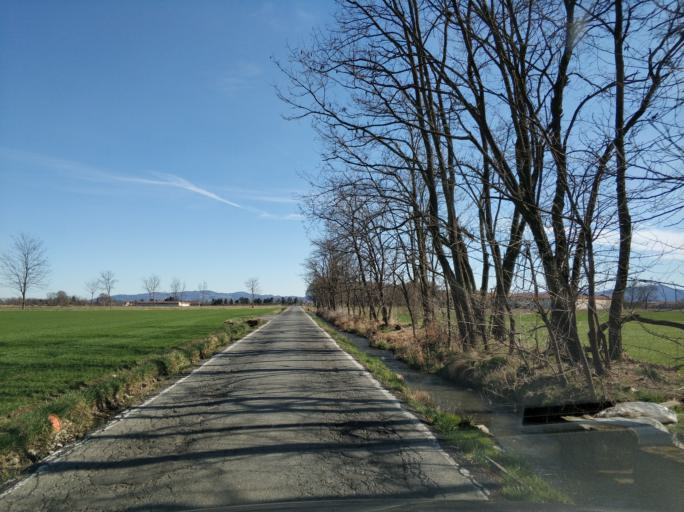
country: IT
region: Piedmont
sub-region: Provincia di Torino
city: Leini
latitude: 45.1956
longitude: 7.6828
